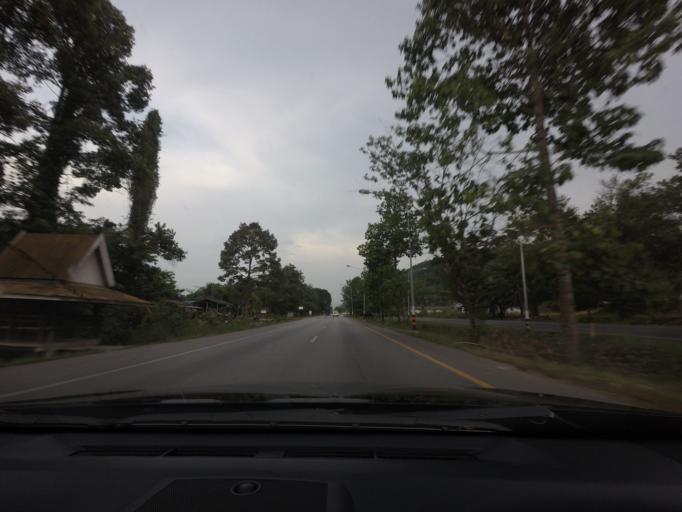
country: TH
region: Surat Thani
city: Tha Chana
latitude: 9.4933
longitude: 99.1357
